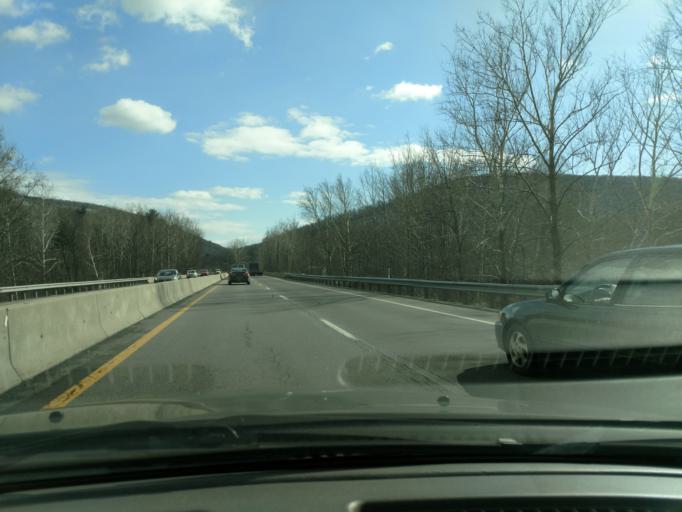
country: US
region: Pennsylvania
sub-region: Berks County
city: West Hamburg
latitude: 40.6071
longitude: -76.0301
